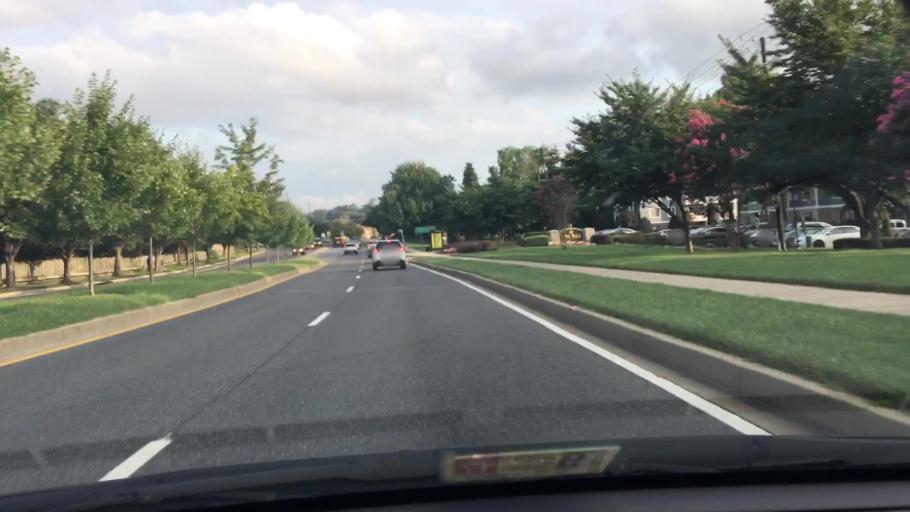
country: US
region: Maryland
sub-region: Montgomery County
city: Germantown
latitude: 39.1848
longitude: -77.2395
